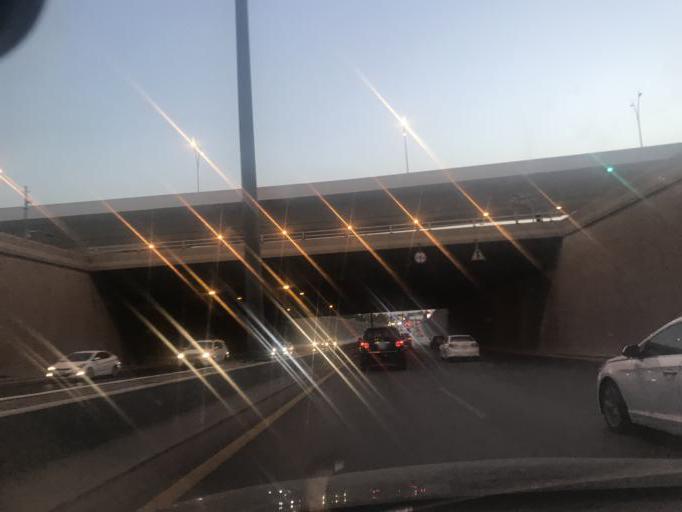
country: SA
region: Ar Riyad
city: Riyadh
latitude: 24.6756
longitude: 46.6791
